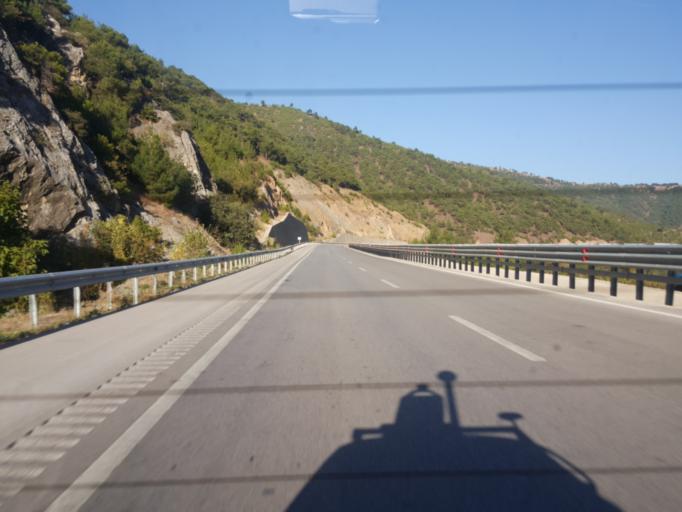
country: TR
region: Amasya
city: Akdag
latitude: 40.7525
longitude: 36.0621
